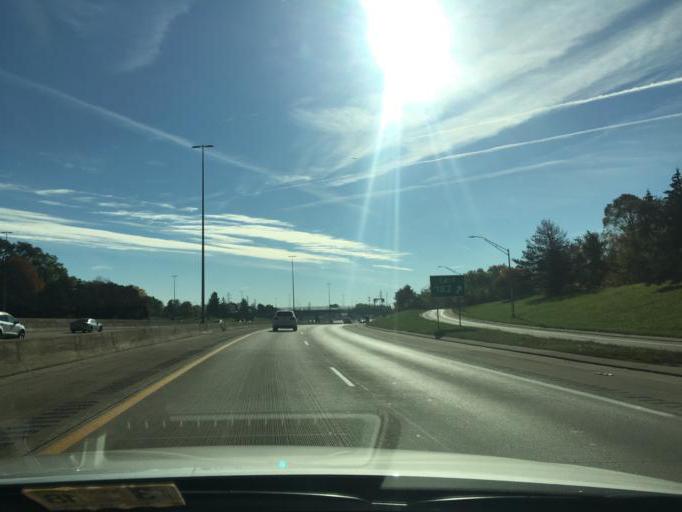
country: US
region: Michigan
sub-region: Wayne County
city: Redford
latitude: 42.3845
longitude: -83.2422
